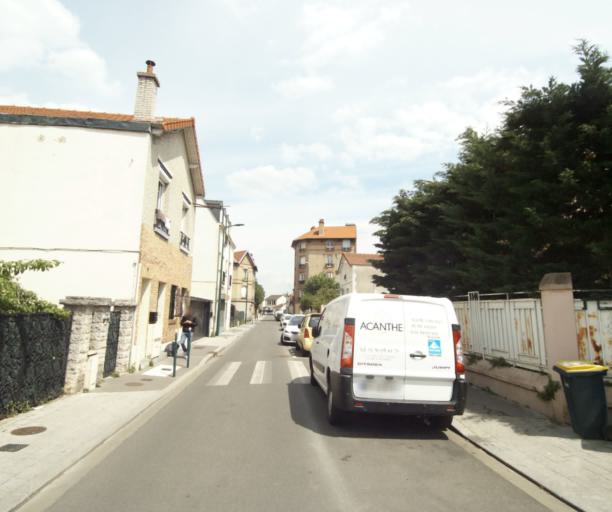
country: FR
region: Ile-de-France
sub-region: Departement des Hauts-de-Seine
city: La Garenne-Colombes
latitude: 48.9165
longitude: 2.2370
